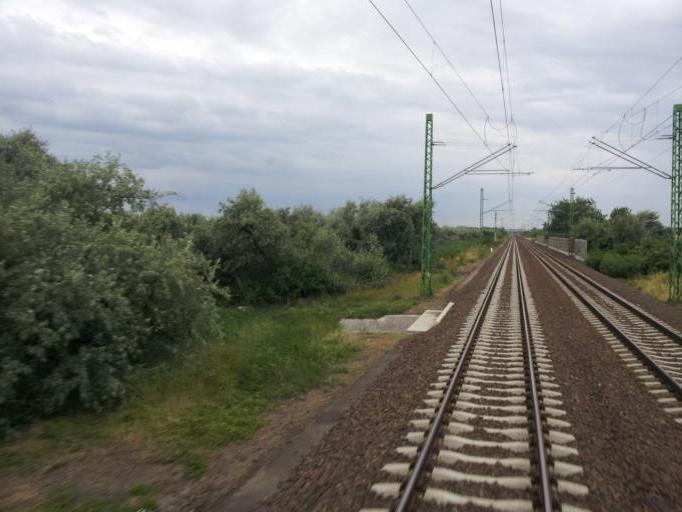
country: HU
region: Fejer
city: Pakozd
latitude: 47.1855
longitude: 18.5754
